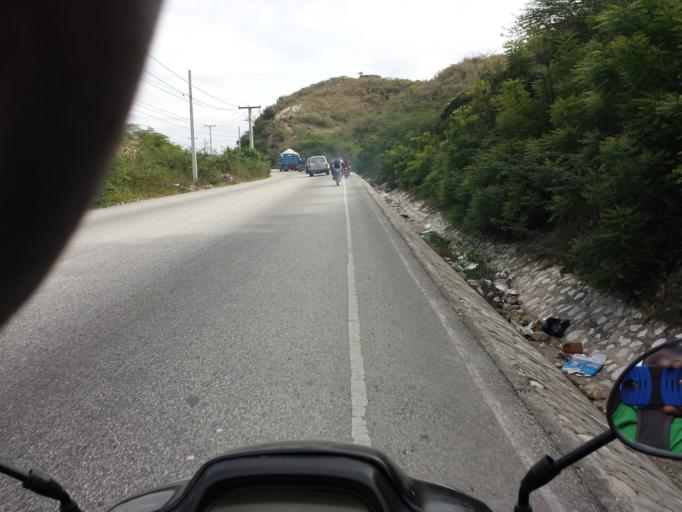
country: HT
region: Artibonite
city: Saint-Marc
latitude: 19.1332
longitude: -72.6783
